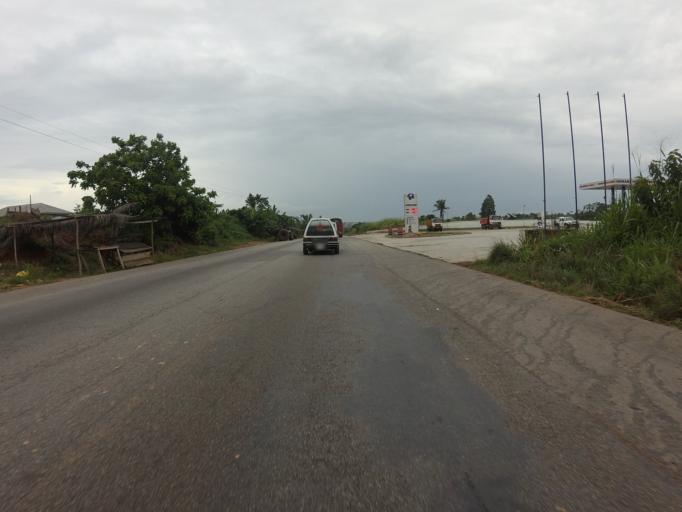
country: GH
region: Ashanti
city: Konongo
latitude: 6.6160
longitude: -1.1622
